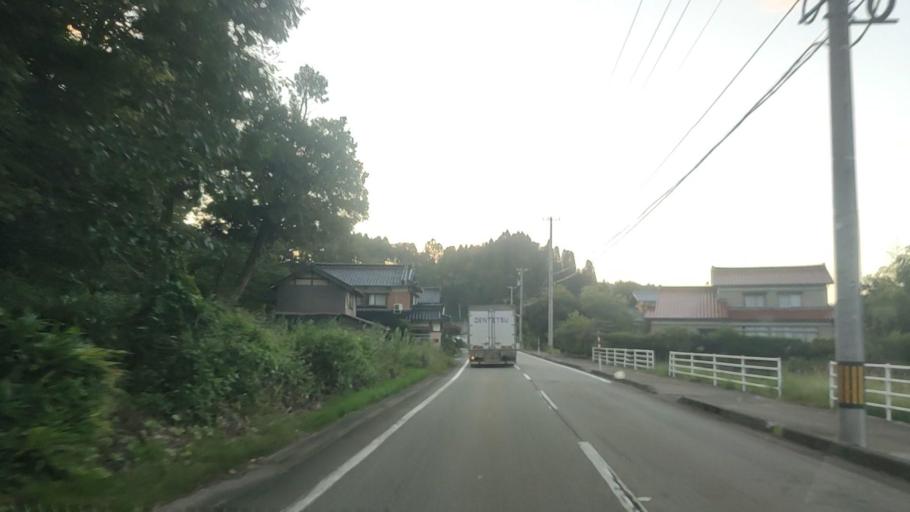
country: JP
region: Ishikawa
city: Tsubata
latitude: 36.6475
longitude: 136.7623
